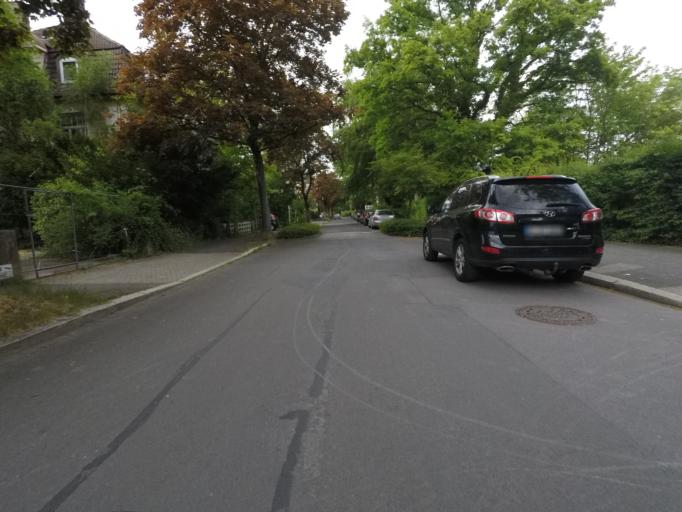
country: DE
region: North Rhine-Westphalia
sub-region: Regierungsbezirk Detmold
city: Bad Salzuflen
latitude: 52.0903
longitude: 8.7518
